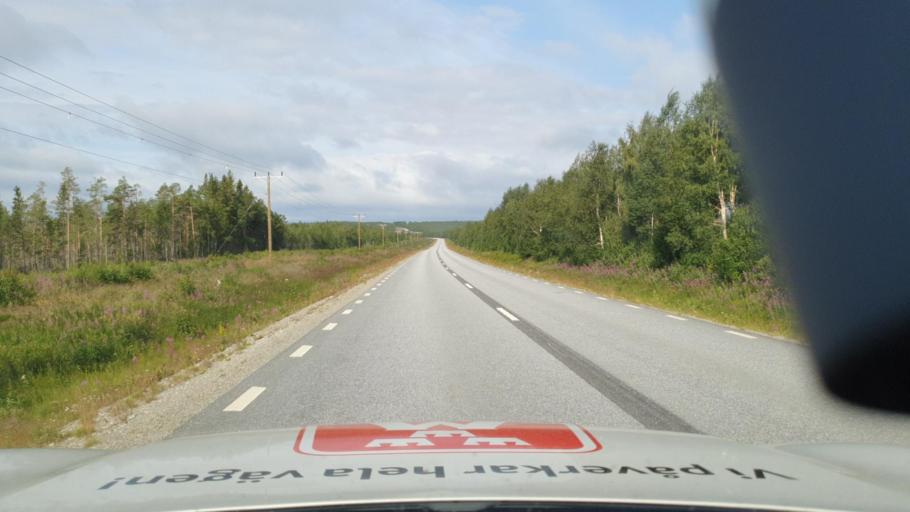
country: SE
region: Vaesterbotten
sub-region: Asele Kommun
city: Insjon
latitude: 64.1971
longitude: 17.5714
